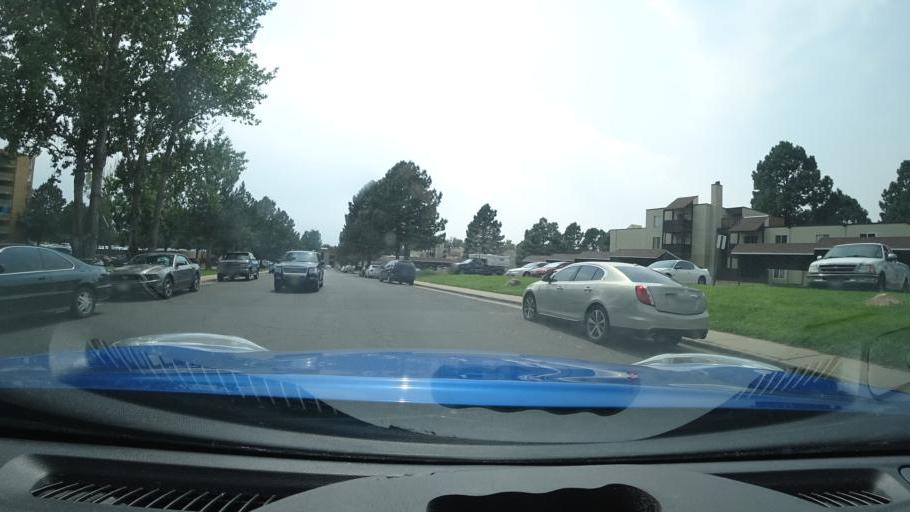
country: US
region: Colorado
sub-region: Adams County
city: Aurora
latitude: 39.6724
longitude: -104.8717
